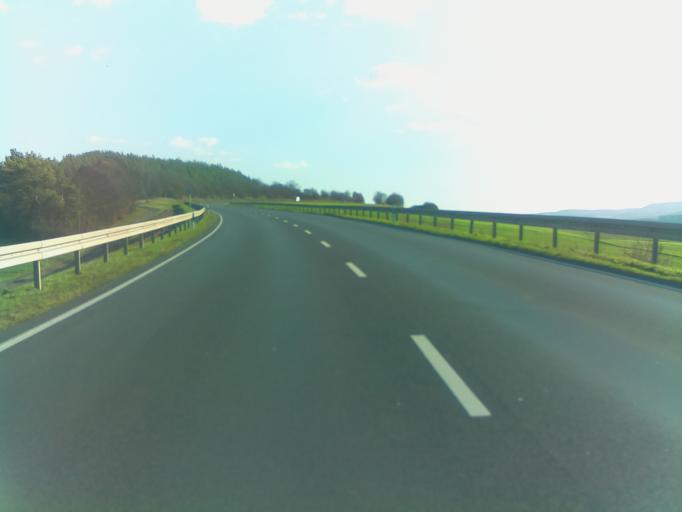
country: DE
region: Bavaria
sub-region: Regierungsbezirk Unterfranken
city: Saal an der Saale
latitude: 50.3097
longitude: 10.3837
